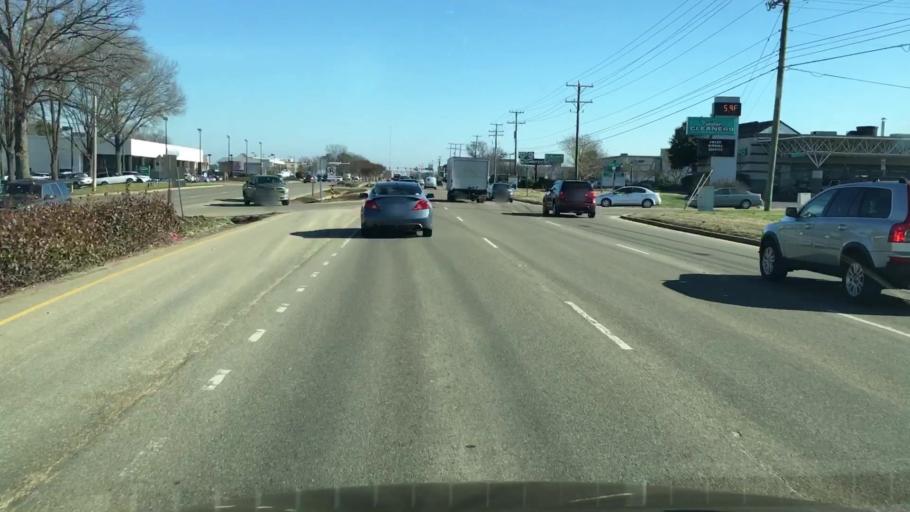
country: US
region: Virginia
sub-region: Chesterfield County
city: Bon Air
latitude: 37.5047
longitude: -77.6160
